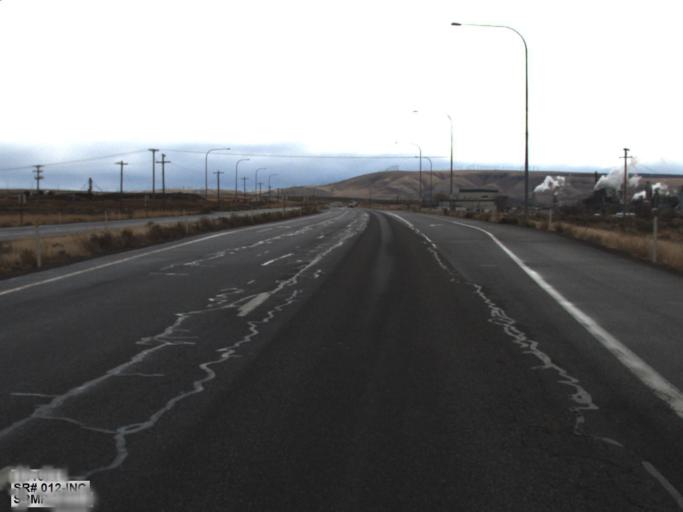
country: US
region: Washington
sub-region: Benton County
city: Finley
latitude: 46.1181
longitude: -118.9261
